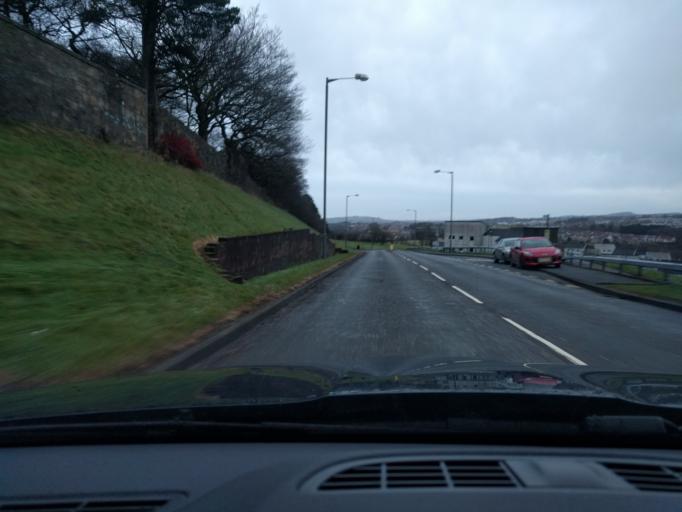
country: GB
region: Scotland
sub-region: Falkirk
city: Falkirk
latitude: 55.9879
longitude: -3.7707
